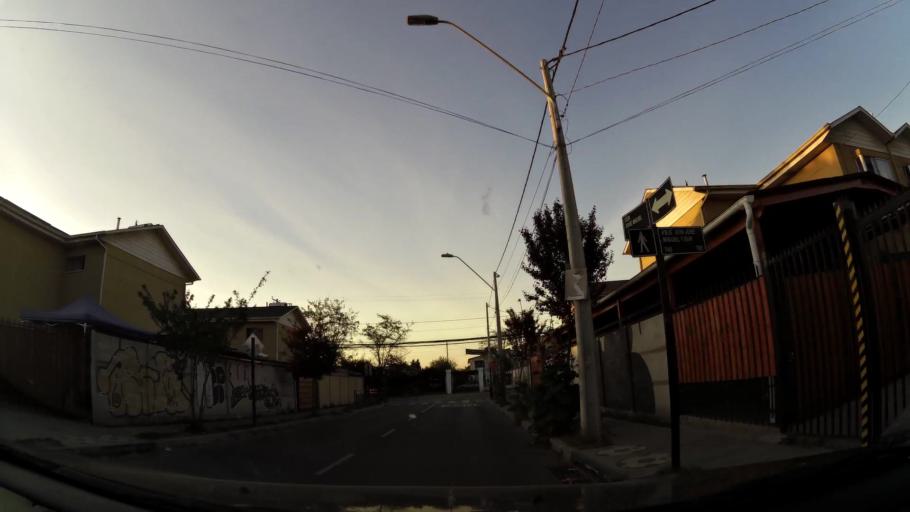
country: CL
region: Santiago Metropolitan
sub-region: Provincia de Cordillera
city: Puente Alto
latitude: -33.6018
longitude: -70.5859
